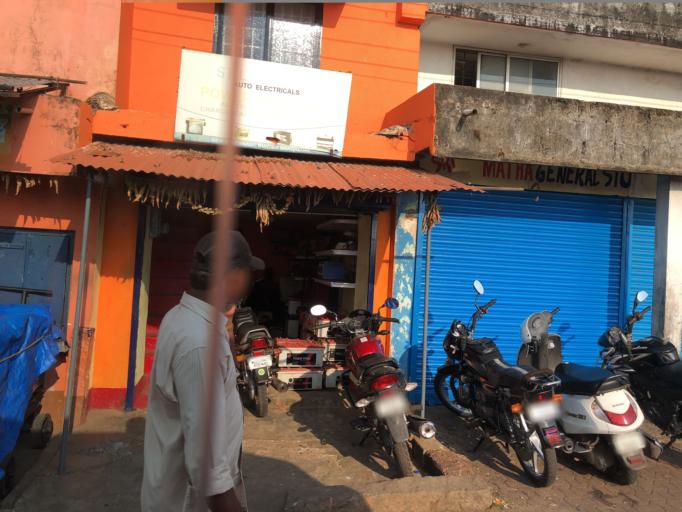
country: IN
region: Karnataka
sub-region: Dakshina Kannada
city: Ullal
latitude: 12.8569
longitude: 74.8330
